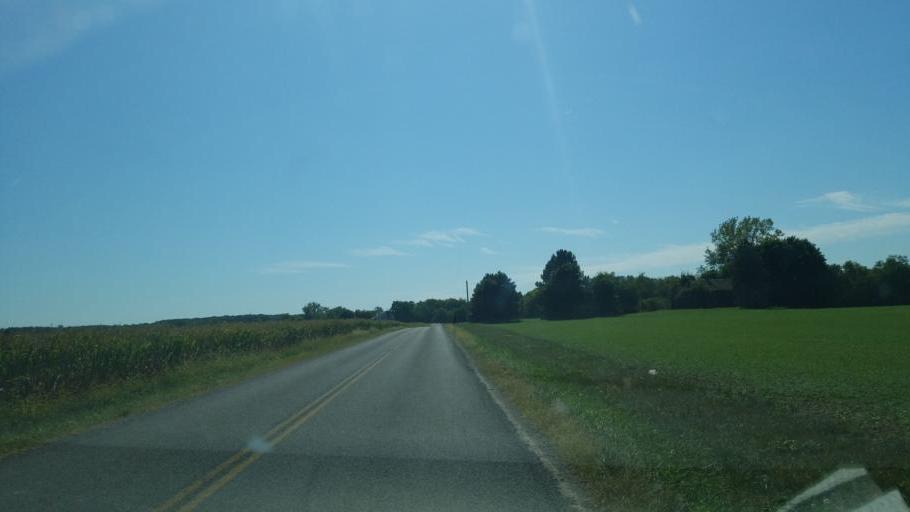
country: US
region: Ohio
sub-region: Logan County
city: Northwood
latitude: 40.4773
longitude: -83.7817
